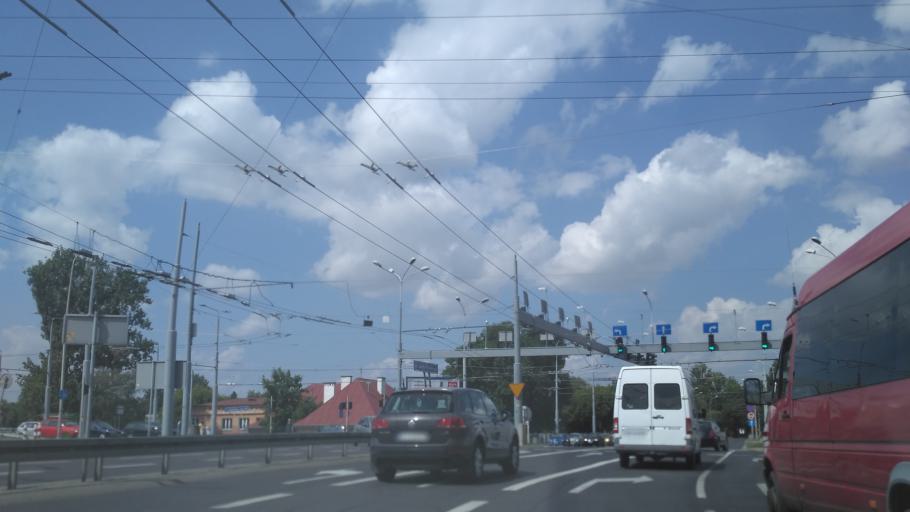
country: PL
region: Lublin Voivodeship
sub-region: Powiat lubelski
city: Lublin
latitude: 51.2346
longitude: 22.5693
